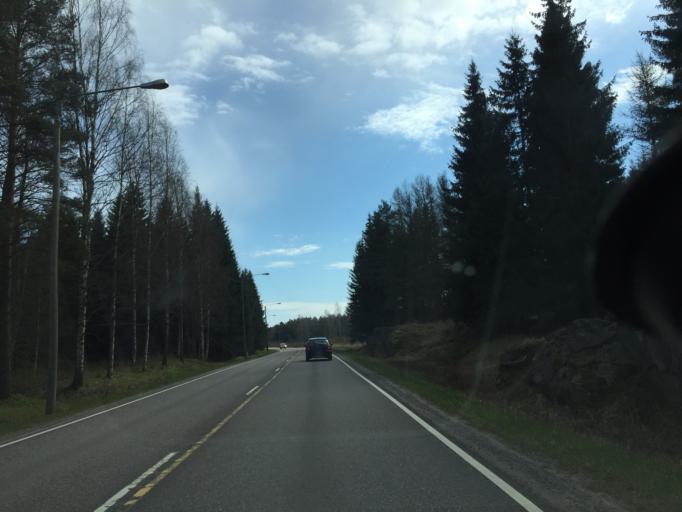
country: FI
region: Uusimaa
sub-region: Raaseporin
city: Ekenaes
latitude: 60.0031
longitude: 23.4022
